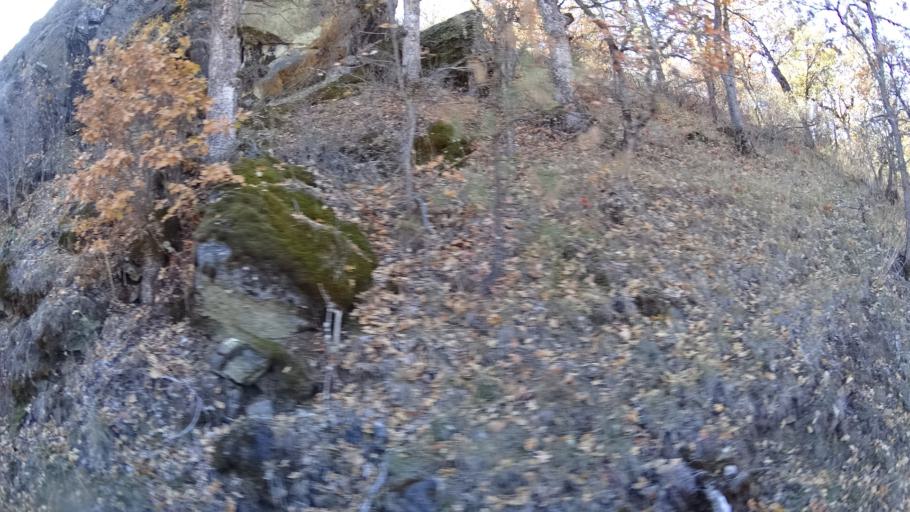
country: US
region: California
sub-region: Siskiyou County
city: Yreka
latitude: 41.8683
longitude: -122.8146
